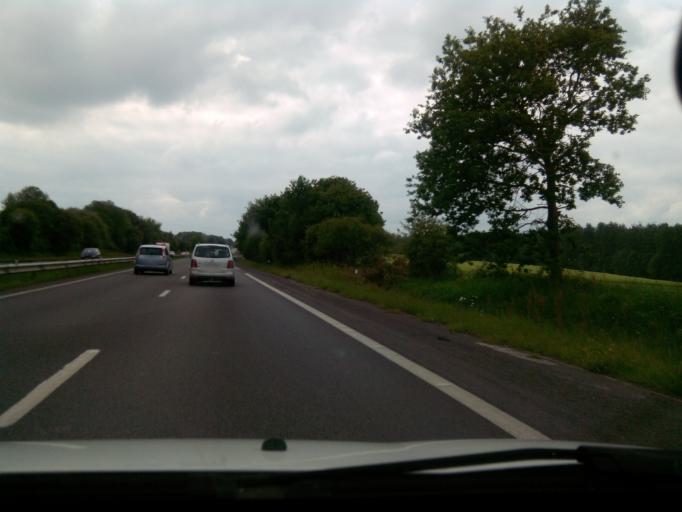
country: FR
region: Brittany
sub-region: Departement des Cotes-d'Armor
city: Caulnes
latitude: 48.2727
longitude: -2.1663
